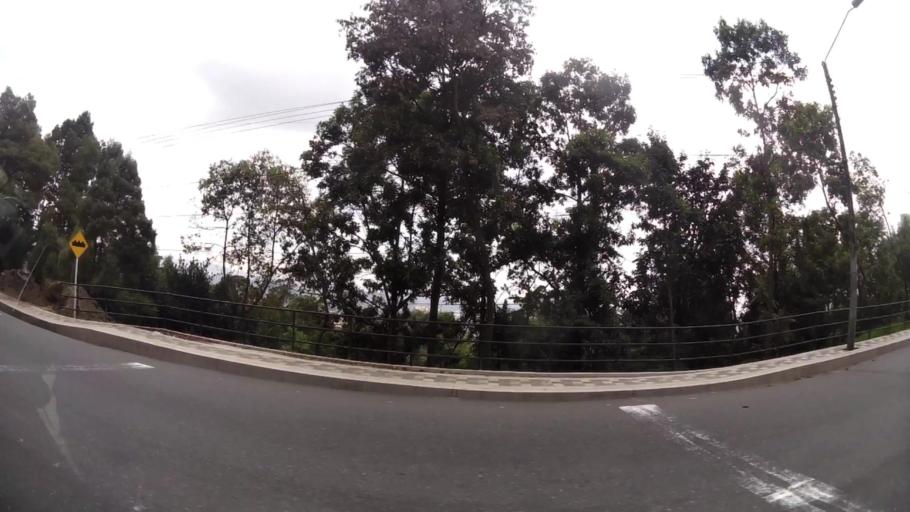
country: CO
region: Bogota D.C.
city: Bogota
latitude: 4.5950
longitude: -74.0673
